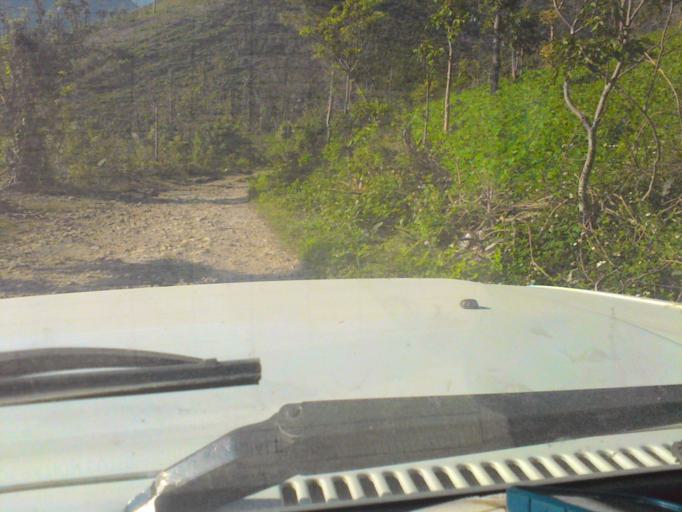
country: HT
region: Grandans
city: Jeremie
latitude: 18.5137
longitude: -74.0829
